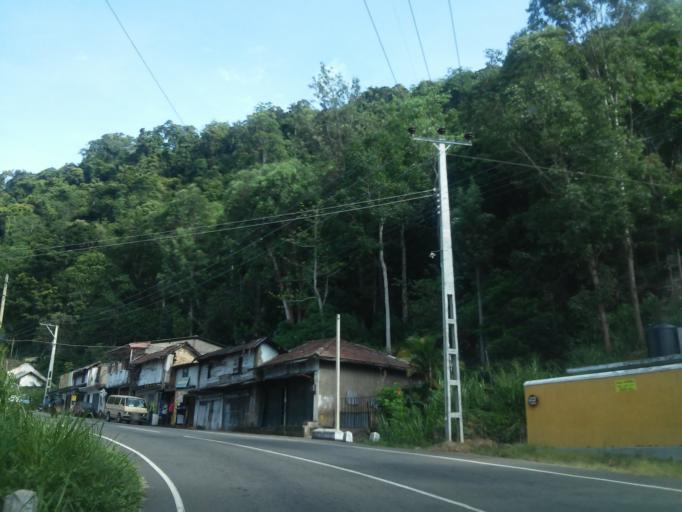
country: LK
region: Uva
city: Haputale
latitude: 6.7655
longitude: 80.8911
